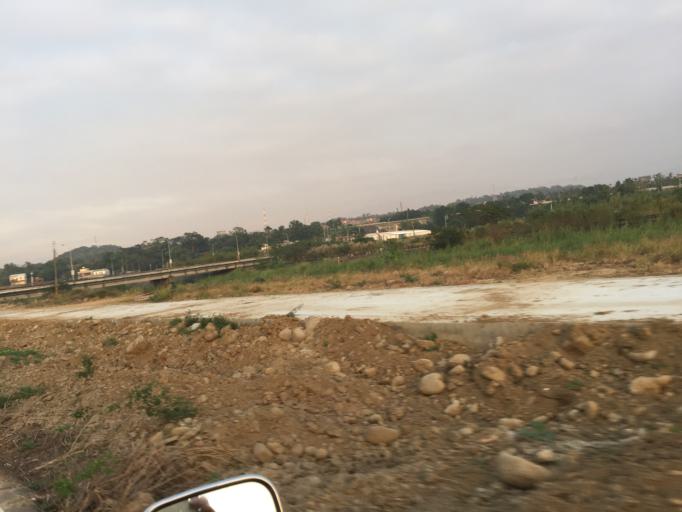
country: TW
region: Taiwan
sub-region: Miaoli
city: Miaoli
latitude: 24.4934
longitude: 120.7790
